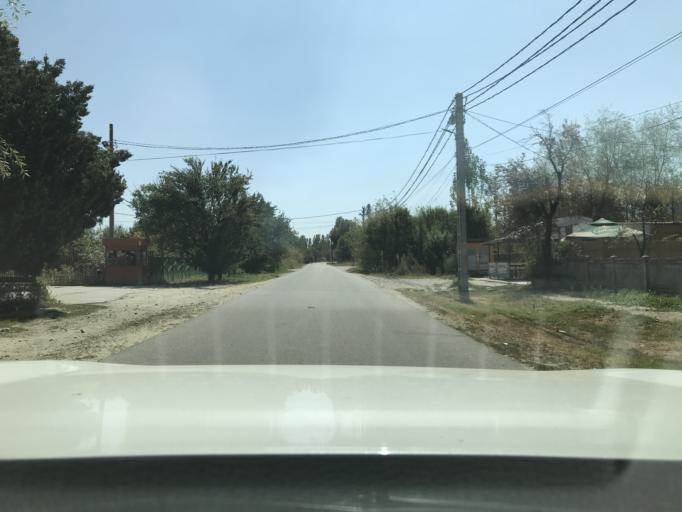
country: RO
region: Olt
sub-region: Comuna Falcoiu
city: Falcoiu
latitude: 44.2400
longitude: 24.3664
